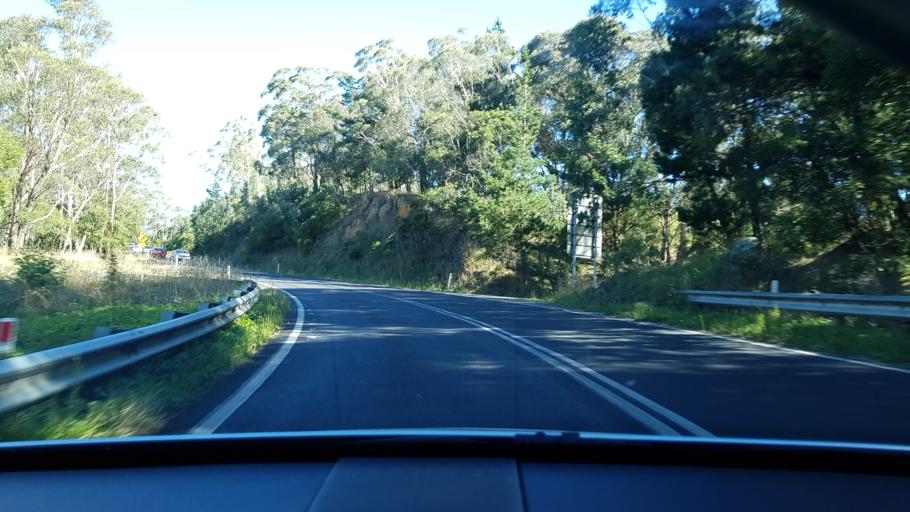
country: AU
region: New South Wales
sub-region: Lithgow
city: Bowenfels
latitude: -33.6587
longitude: 150.0524
